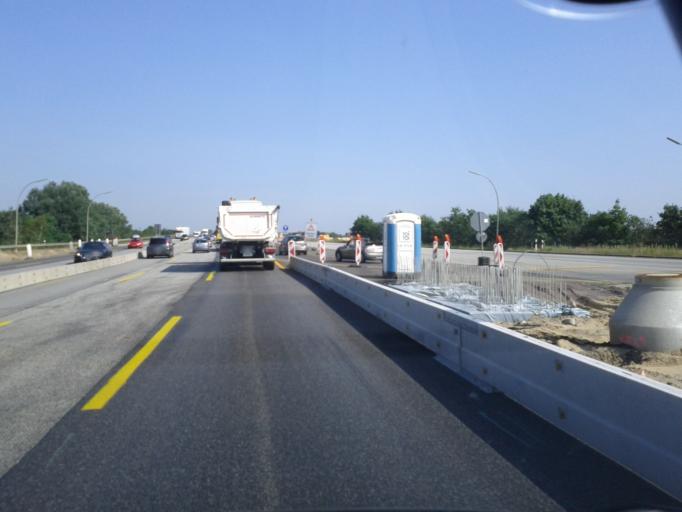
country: DE
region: Hamburg
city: Stellingen
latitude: 53.5846
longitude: 9.9158
